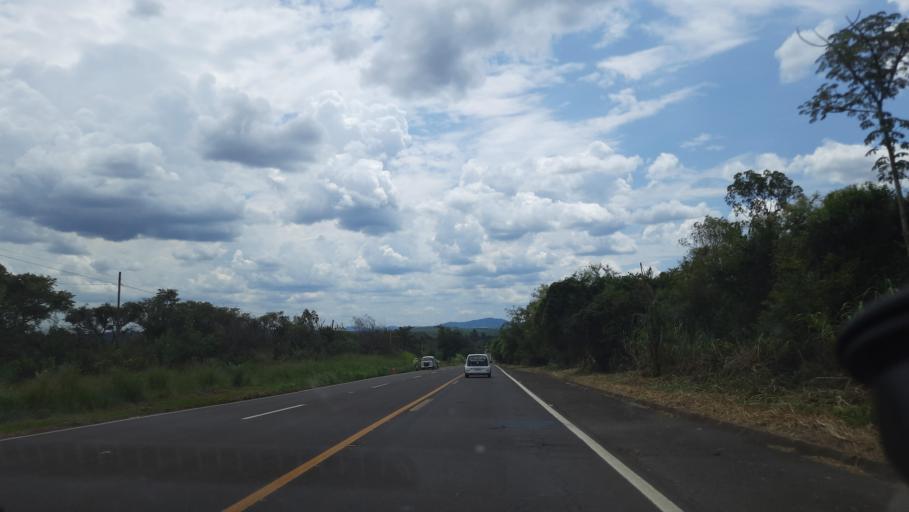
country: BR
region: Sao Paulo
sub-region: Mococa
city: Mococa
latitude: -21.4791
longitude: -47.0867
